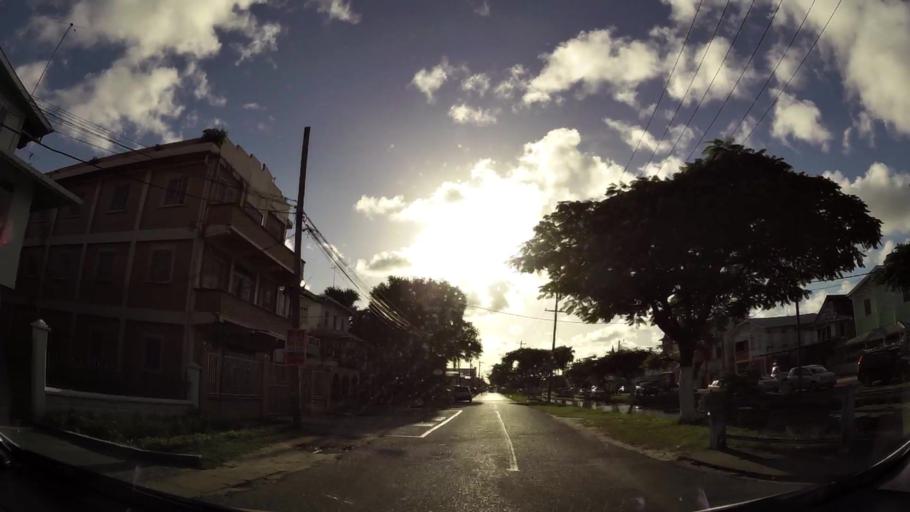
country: GY
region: Demerara-Mahaica
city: Georgetown
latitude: 6.8067
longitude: -58.1544
